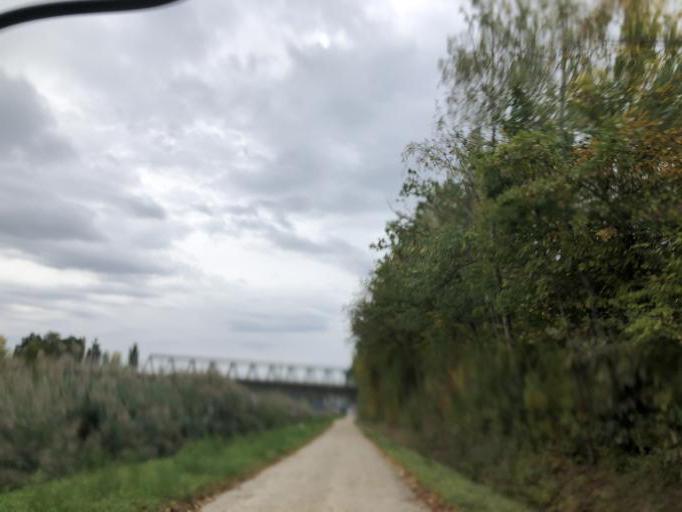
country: DE
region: Bavaria
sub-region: Regierungsbezirk Mittelfranken
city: Erlangen
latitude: 49.5672
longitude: 10.9702
